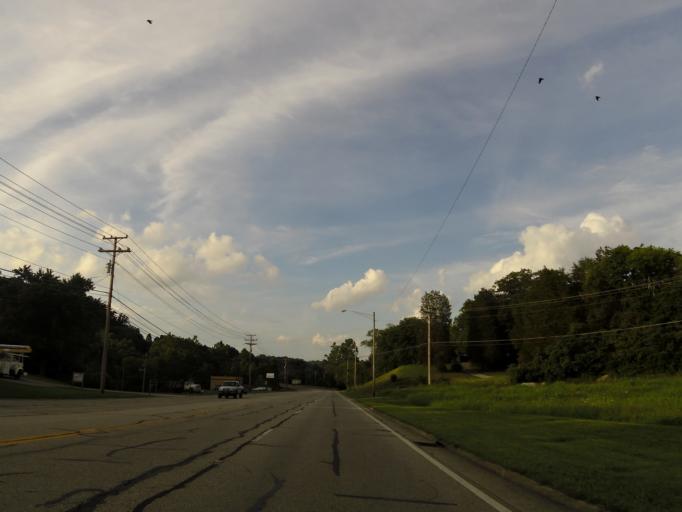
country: US
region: Tennessee
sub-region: Anderson County
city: Clinton
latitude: 36.0777
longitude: -84.1635
